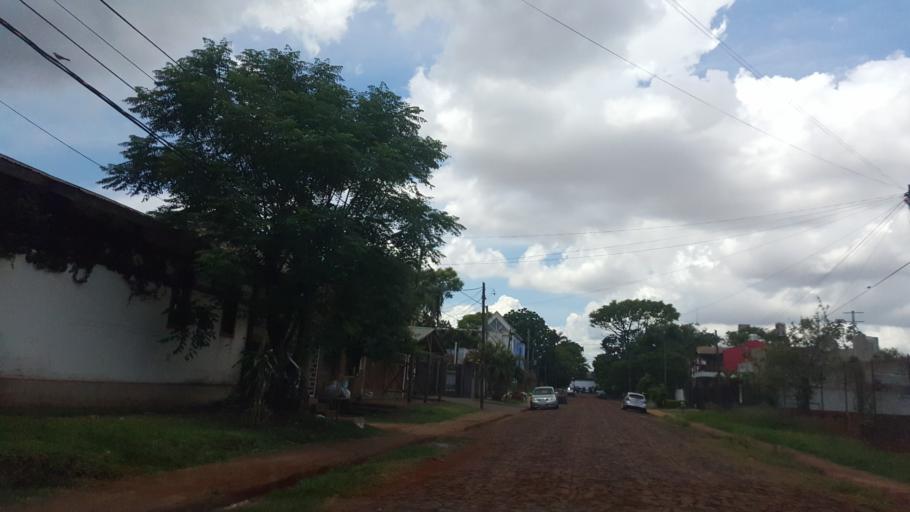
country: AR
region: Misiones
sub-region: Departamento de Capital
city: Posadas
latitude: -27.3950
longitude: -55.9152
